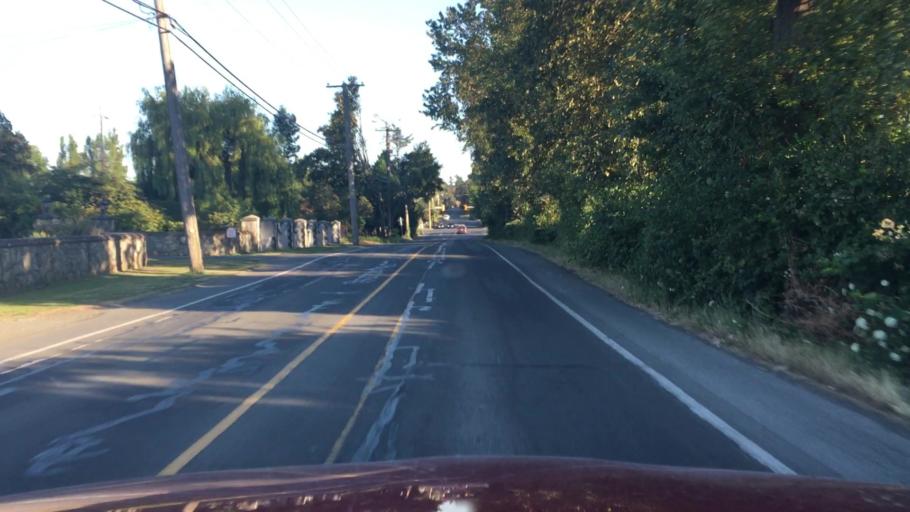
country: CA
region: British Columbia
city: Victoria
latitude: 48.4741
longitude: -123.3518
